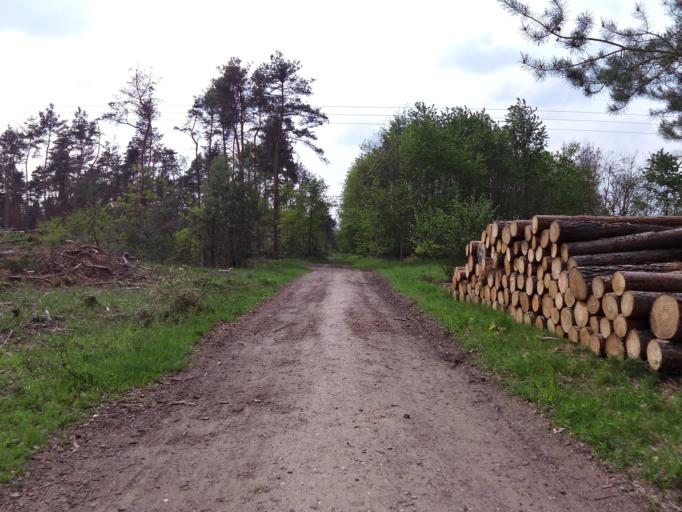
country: DE
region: Rheinland-Pfalz
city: Hassloch
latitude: 49.3496
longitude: 8.2282
